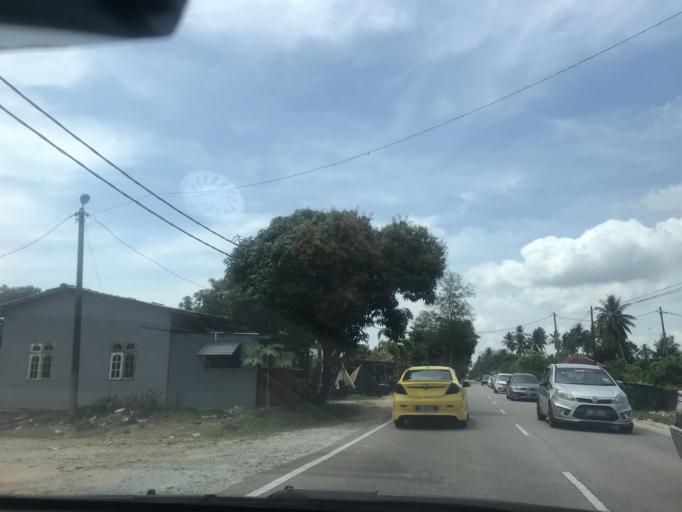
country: MY
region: Kelantan
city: Tumpat
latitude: 6.2096
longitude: 102.1374
